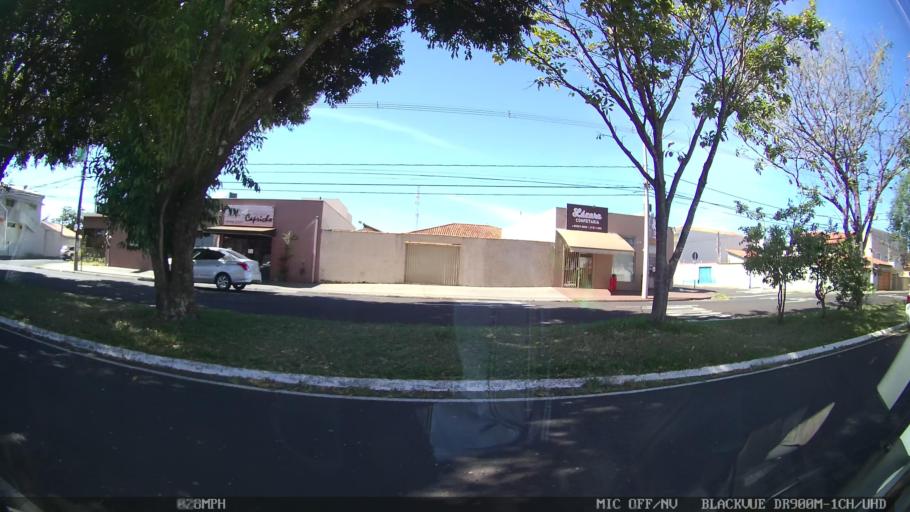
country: BR
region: Sao Paulo
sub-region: Franca
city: Franca
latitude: -20.5599
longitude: -47.3736
